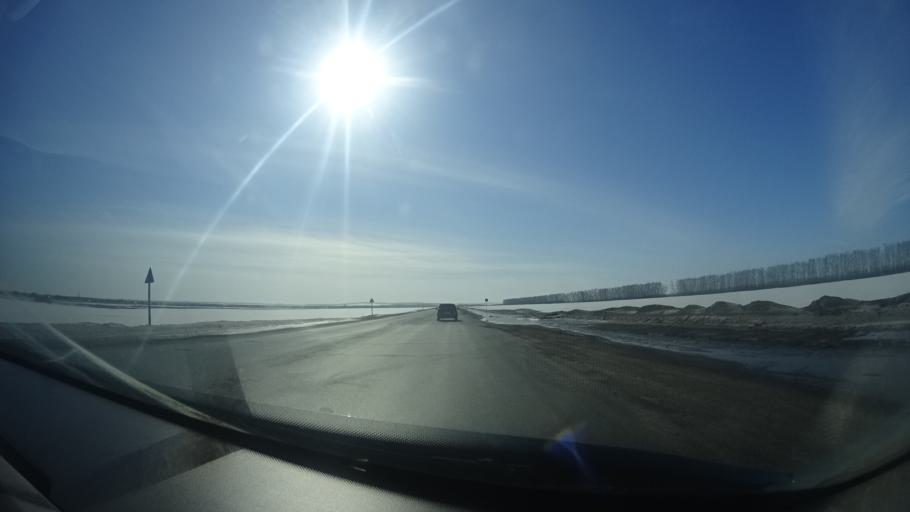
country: RU
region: Bashkortostan
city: Mikhaylovka
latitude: 54.9463
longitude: 55.7505
